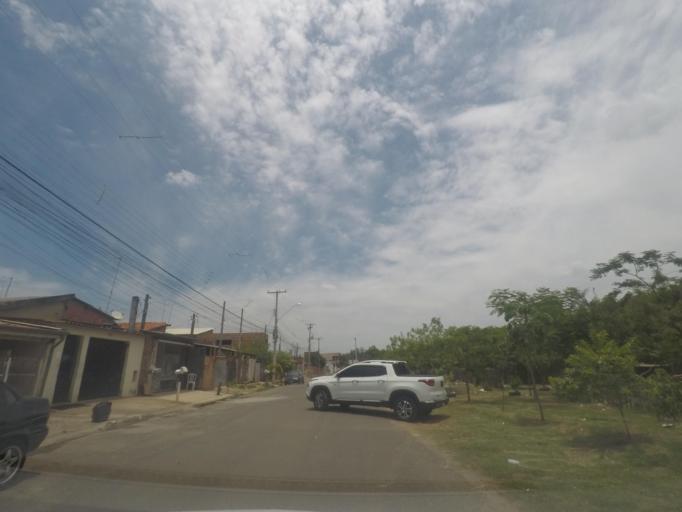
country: BR
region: Sao Paulo
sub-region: Nova Odessa
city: Nova Odessa
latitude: -22.7906
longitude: -47.2787
